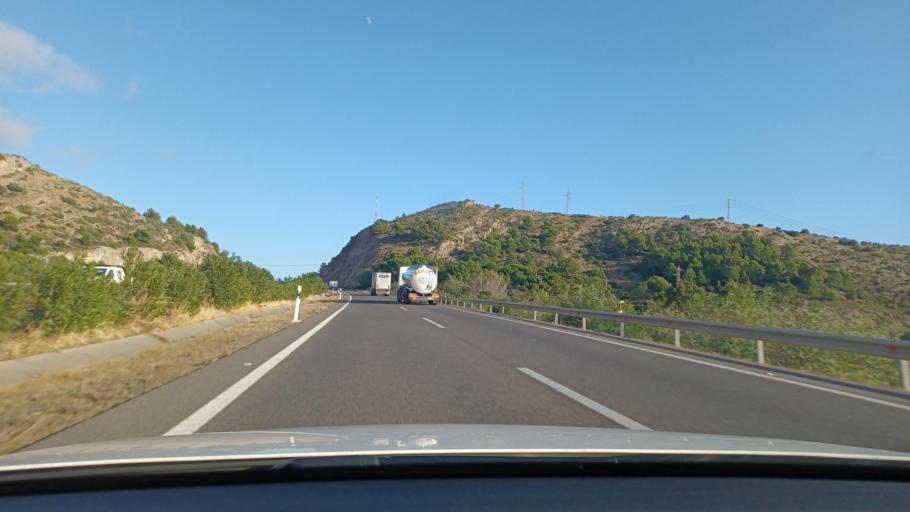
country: ES
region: Valencia
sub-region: Provincia de Castello
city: Benicassim
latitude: 40.0661
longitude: 0.0837
